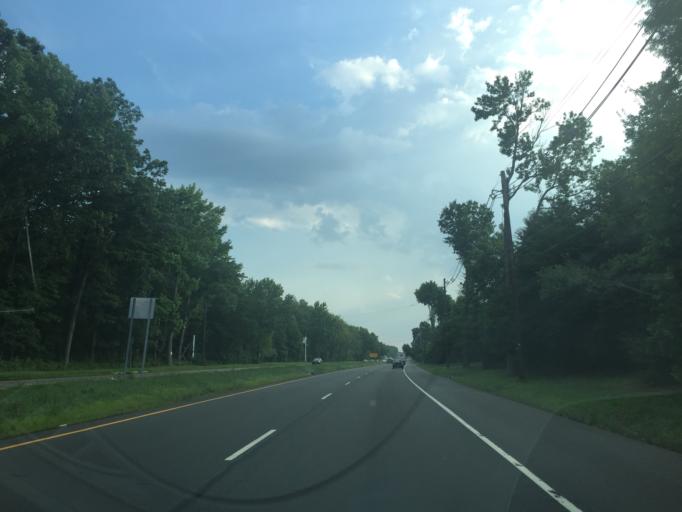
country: US
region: New Jersey
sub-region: Middlesex County
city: Cranbury
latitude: 40.2992
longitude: -74.5138
